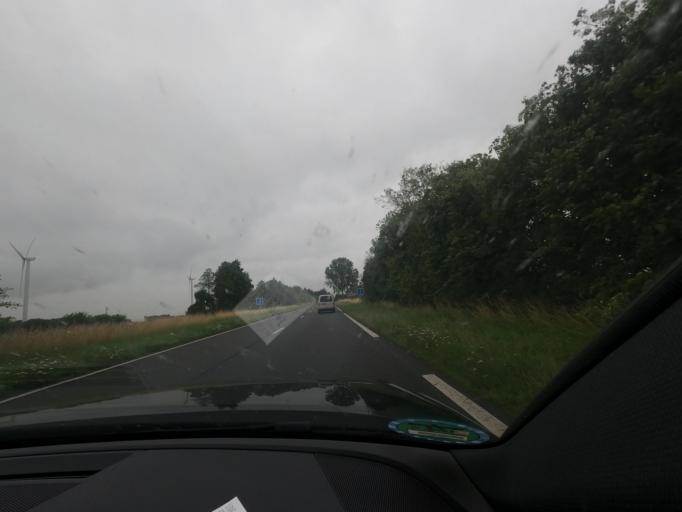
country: FR
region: Picardie
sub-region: Departement de la Somme
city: Roye
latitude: 49.7275
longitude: 2.7192
